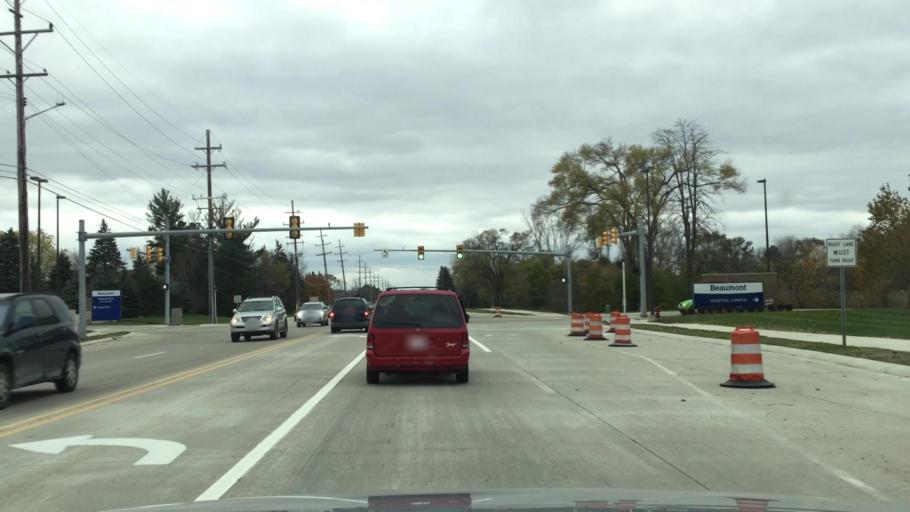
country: US
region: Michigan
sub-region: Macomb County
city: Utica
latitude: 42.6168
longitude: -83.0912
